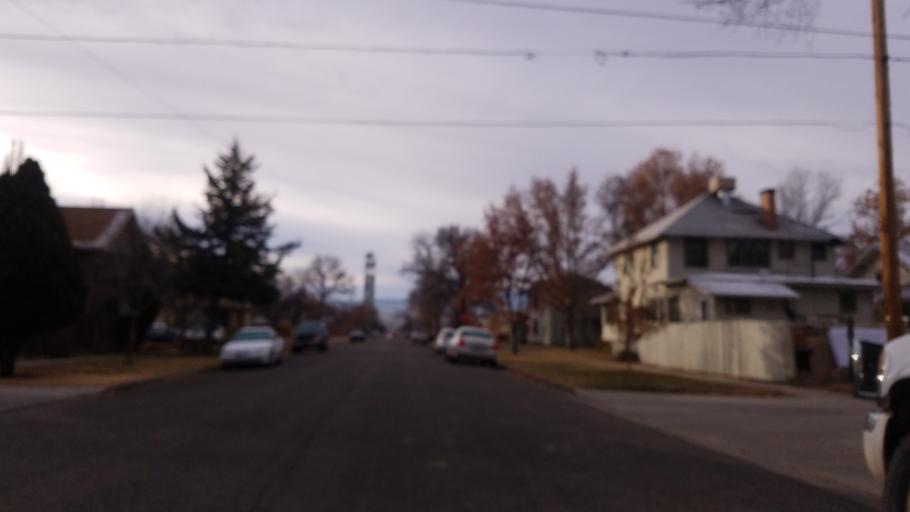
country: US
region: Colorado
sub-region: Mesa County
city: Grand Junction
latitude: 39.0720
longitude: -108.5594
